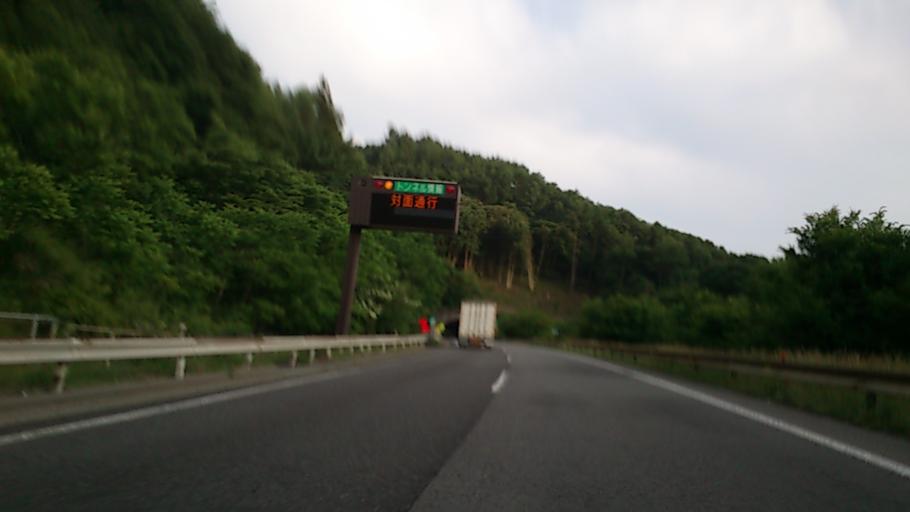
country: JP
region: Nagano
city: Tatsuno
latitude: 36.0027
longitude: 138.0083
